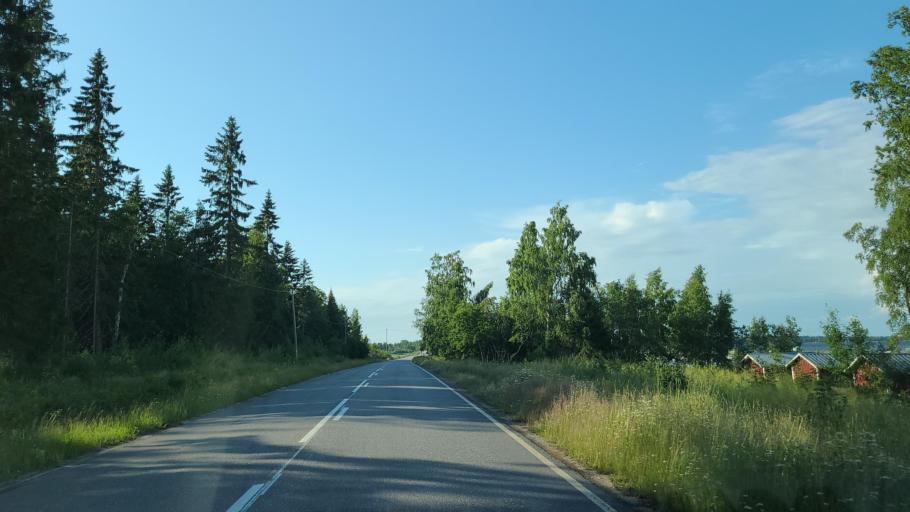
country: FI
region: Ostrobothnia
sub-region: Vaasa
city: Replot
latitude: 63.2694
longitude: 21.3468
